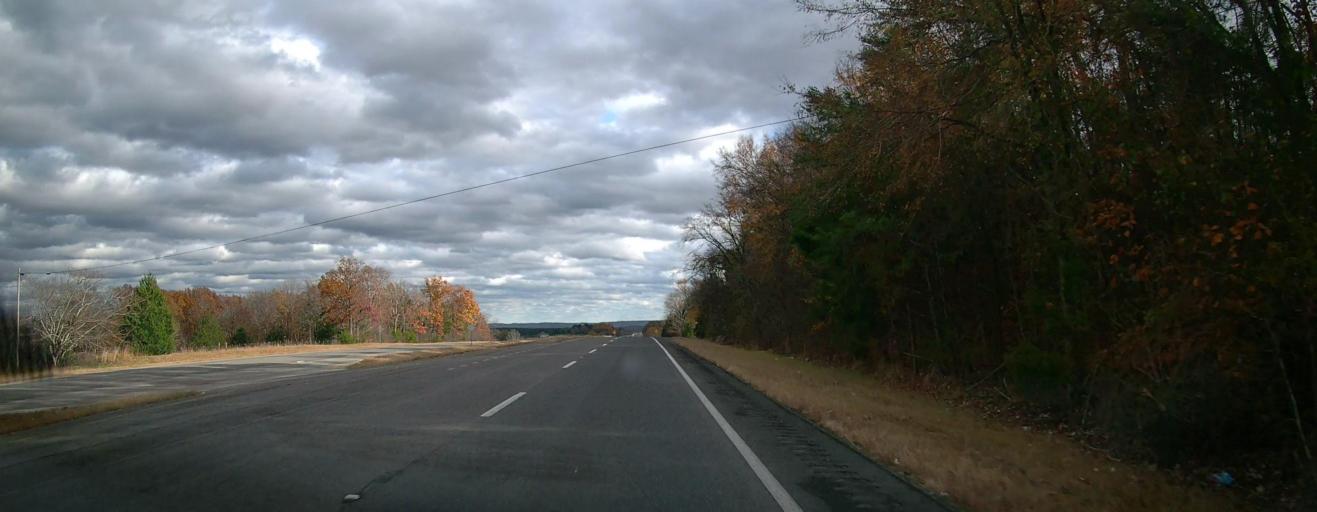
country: US
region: Alabama
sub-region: Morgan County
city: Danville
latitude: 34.3976
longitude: -87.1269
